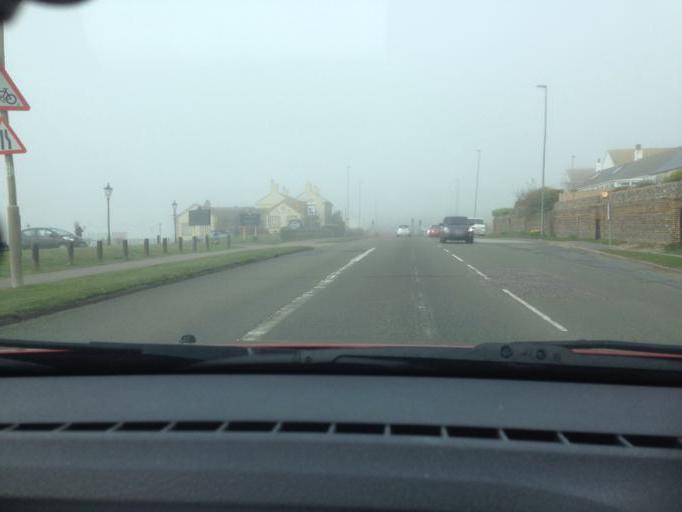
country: GB
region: England
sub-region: East Sussex
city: Peacehaven
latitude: 50.7950
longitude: -0.0191
